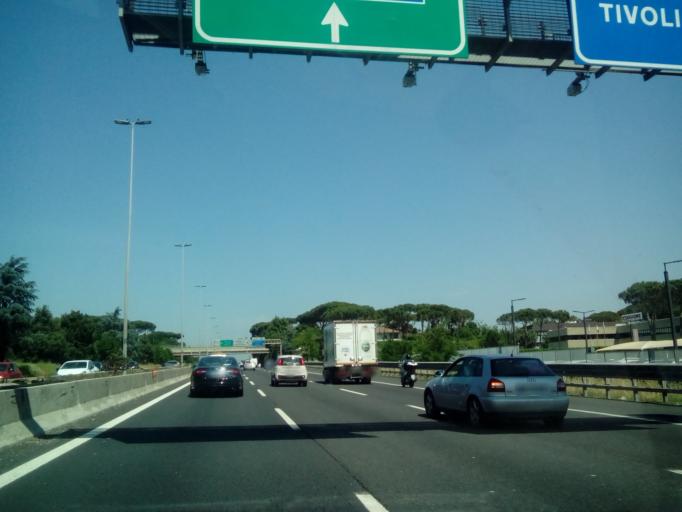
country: IT
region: Latium
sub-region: Citta metropolitana di Roma Capitale
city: Setteville
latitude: 41.9279
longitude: 12.6056
